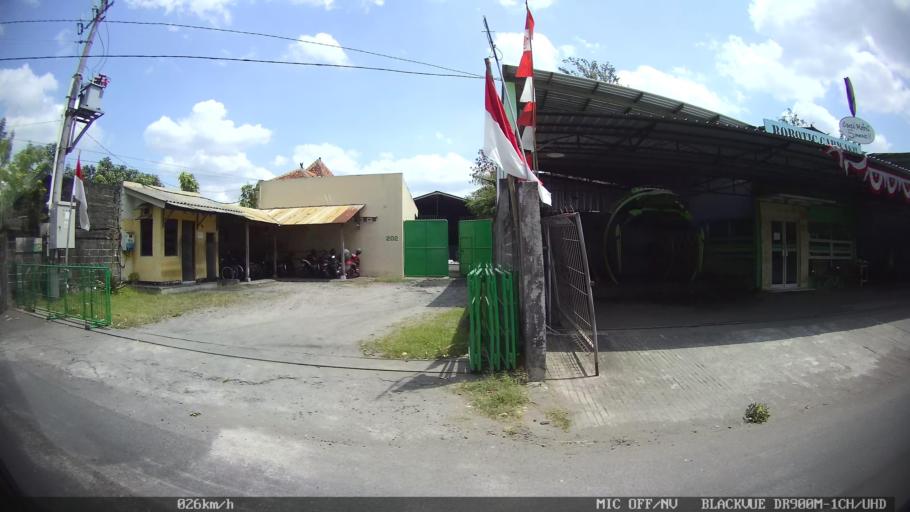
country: ID
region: Daerah Istimewa Yogyakarta
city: Kasihan
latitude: -7.8247
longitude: 110.3471
